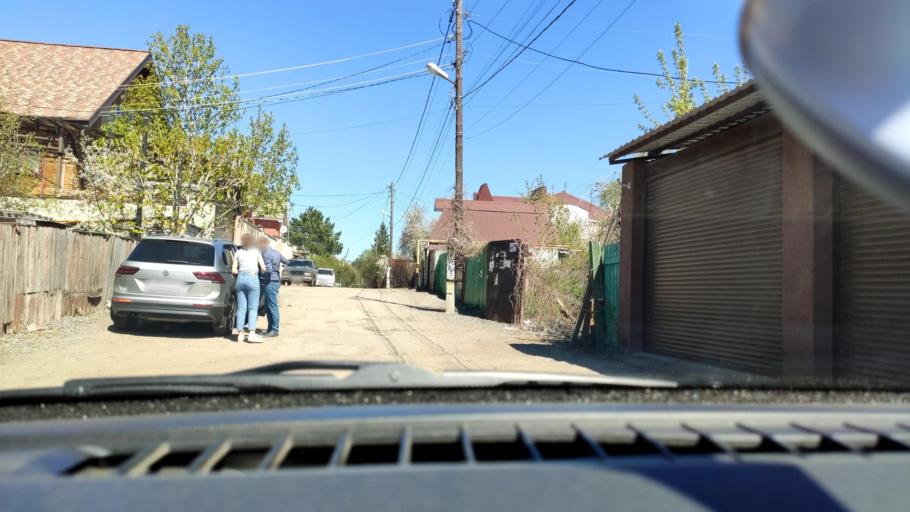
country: RU
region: Samara
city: Samara
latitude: 53.2568
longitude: 50.1911
